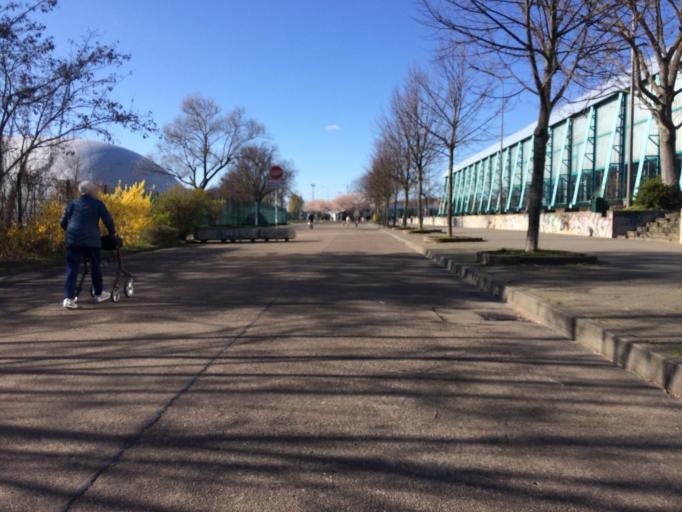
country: DE
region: Berlin
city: Fennpfuhl
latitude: 52.5391
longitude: 13.4807
